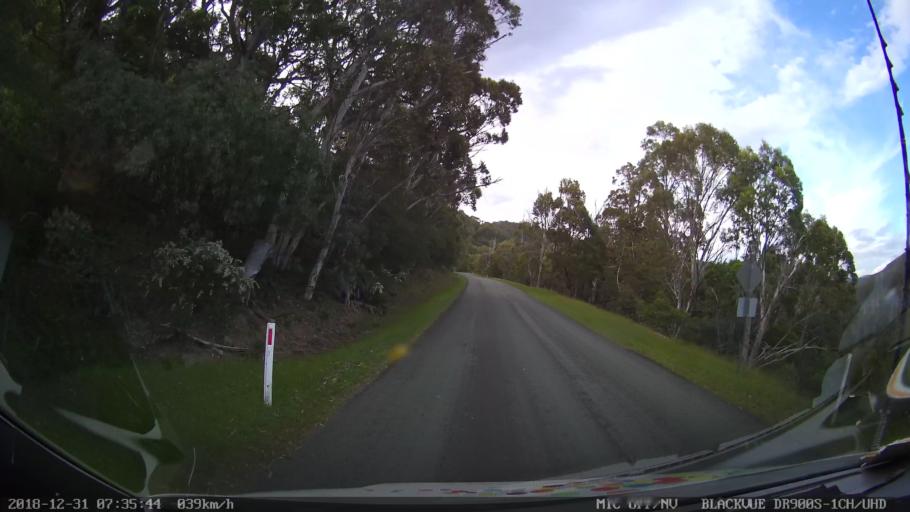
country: AU
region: New South Wales
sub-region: Snowy River
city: Jindabyne
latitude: -36.3364
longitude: 148.4441
